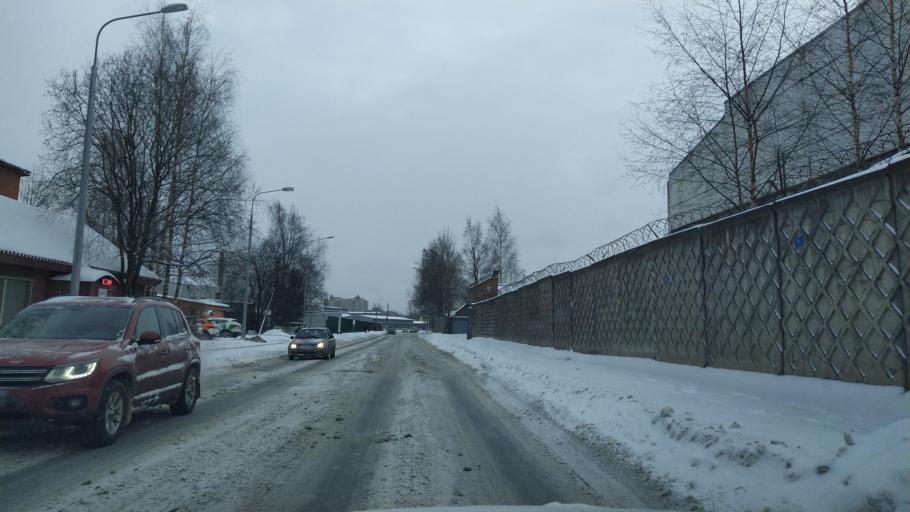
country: RU
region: St.-Petersburg
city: Komendantsky aerodrom
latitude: 59.9931
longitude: 30.2760
